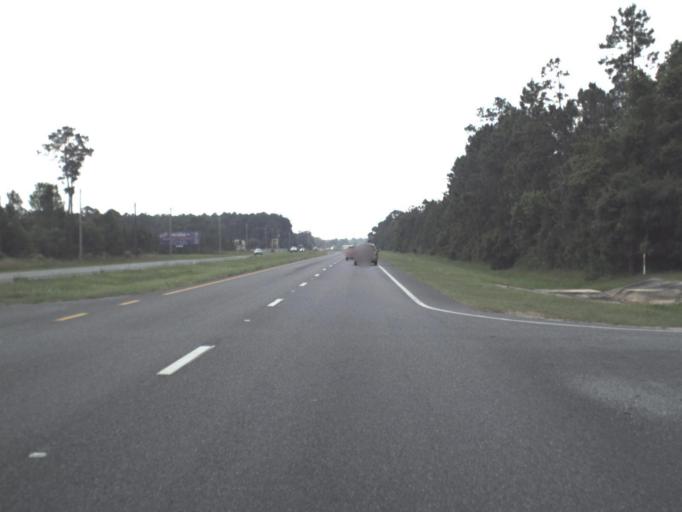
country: US
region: Florida
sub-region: Putnam County
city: Palatka
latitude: 29.6818
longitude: -81.6615
